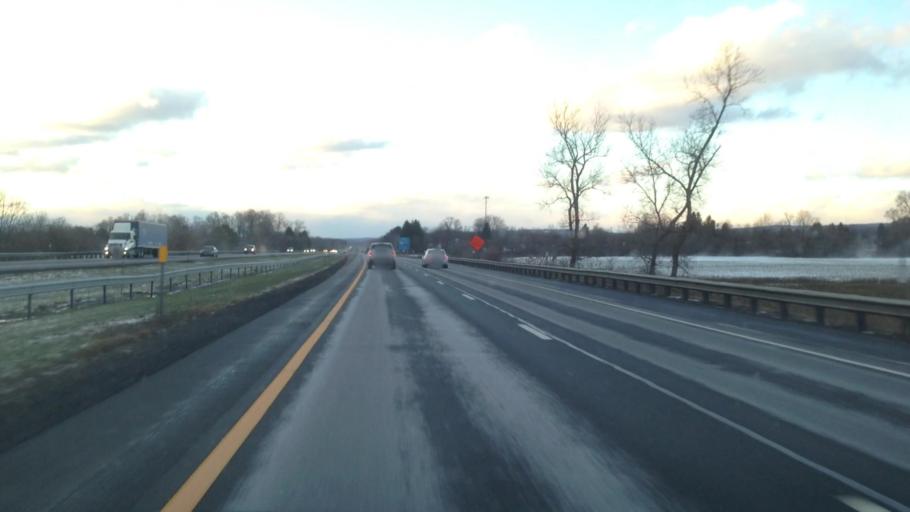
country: US
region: New York
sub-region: Herkimer County
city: Frankfort
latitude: 43.0593
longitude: -75.0732
